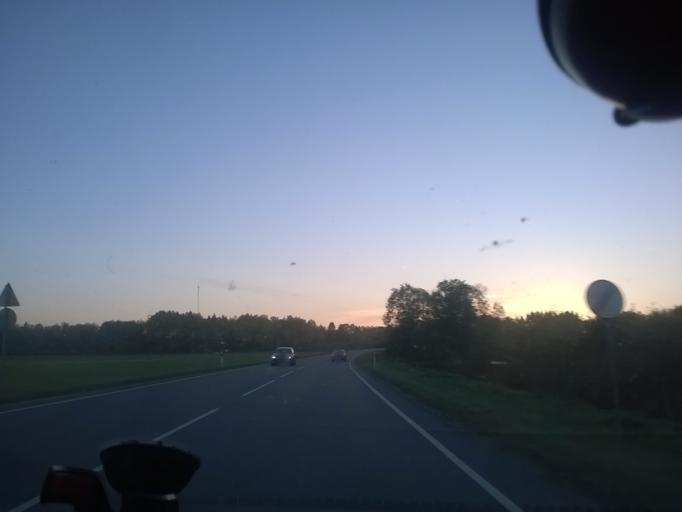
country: EE
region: Laeaene
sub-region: Ridala Parish
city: Uuemoisa
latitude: 58.9613
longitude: 23.8206
